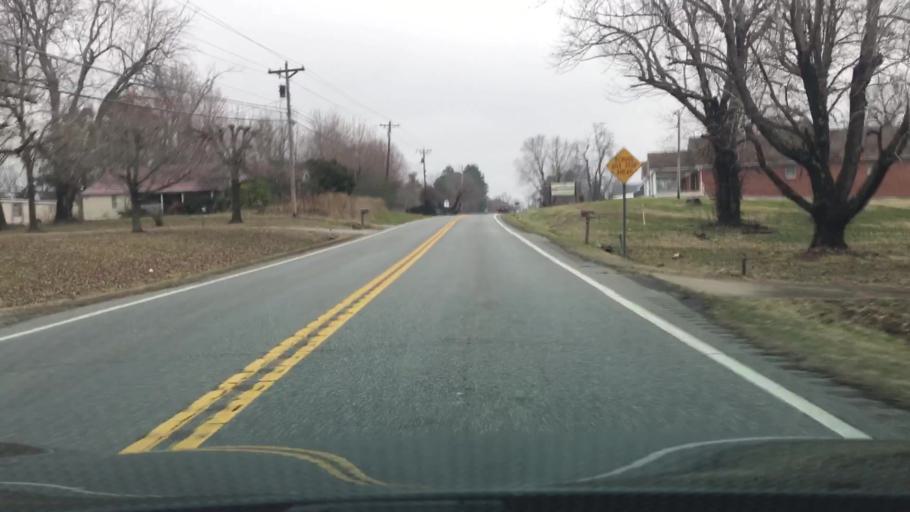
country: US
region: Kentucky
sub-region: Marshall County
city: Calvert City
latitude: 36.9581
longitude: -88.3742
